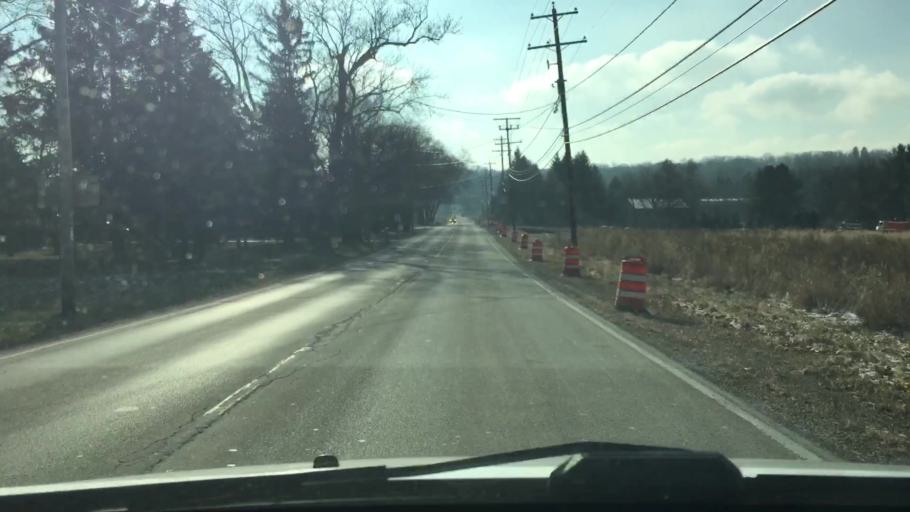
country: US
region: Wisconsin
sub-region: Waukesha County
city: Waukesha
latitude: 42.9975
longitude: -88.2902
